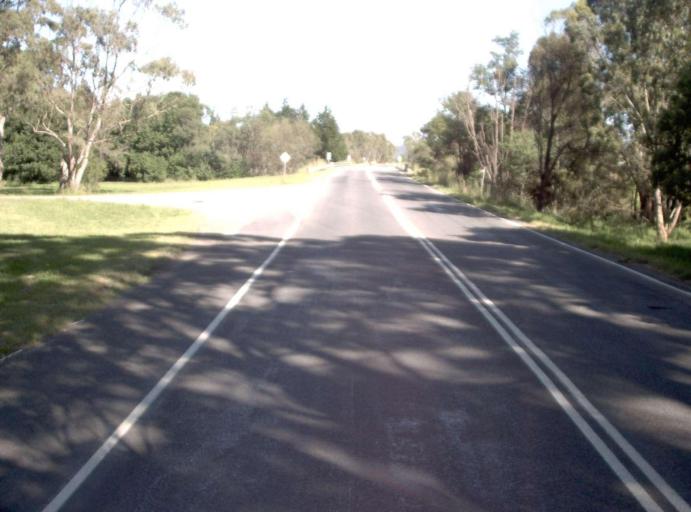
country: AU
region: Victoria
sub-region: Latrobe
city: Traralgon
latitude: -38.1706
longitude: 146.4935
